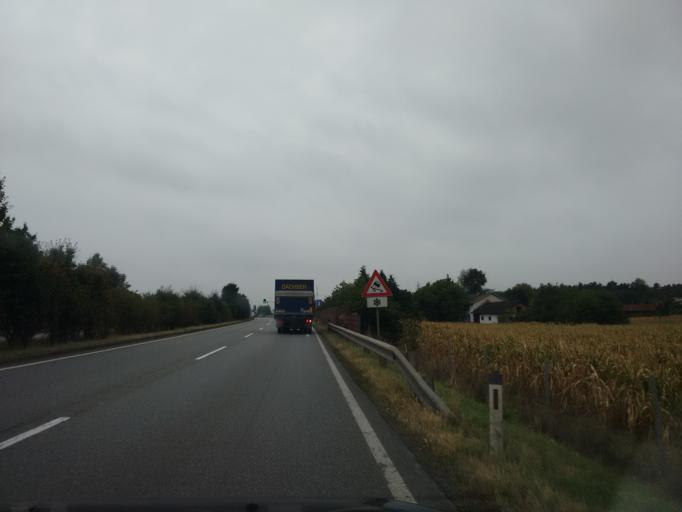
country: AT
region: Upper Austria
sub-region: Wels-Land
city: Marchtrenk
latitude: 48.1888
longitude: 14.0893
